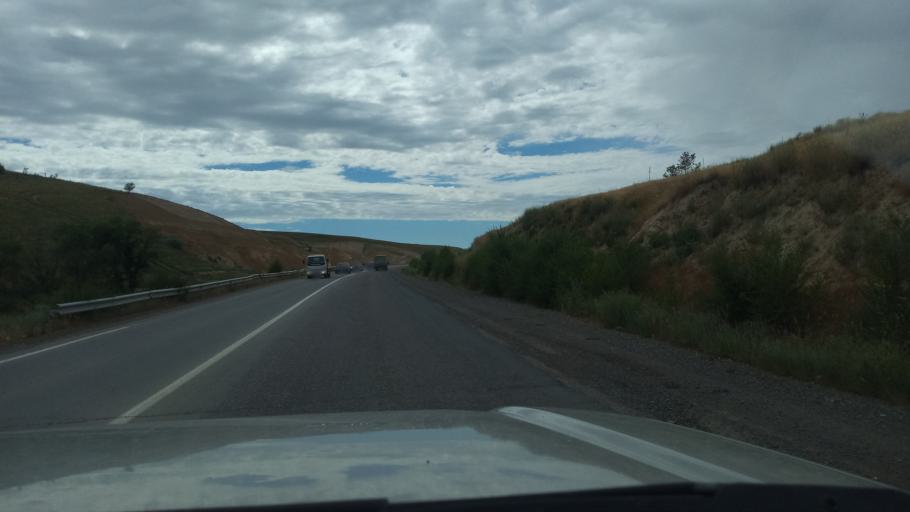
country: KZ
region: Almaty Oblysy
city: Burunday
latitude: 43.2900
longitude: 76.2491
